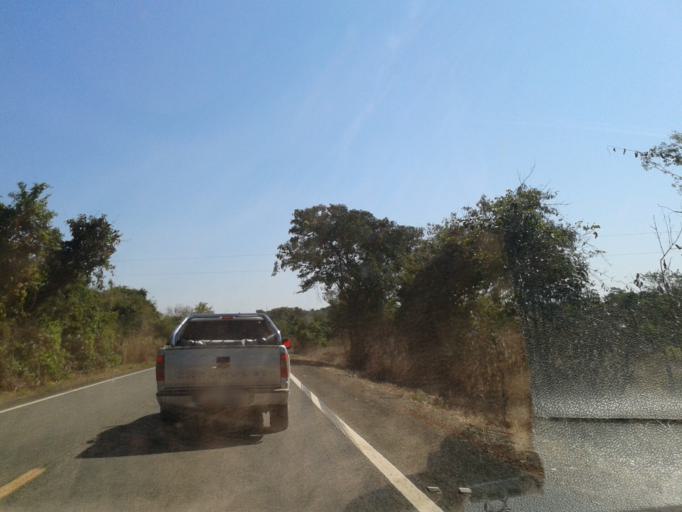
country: BR
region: Goias
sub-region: Sao Miguel Do Araguaia
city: Sao Miguel do Araguaia
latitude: -13.8836
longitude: -50.3298
